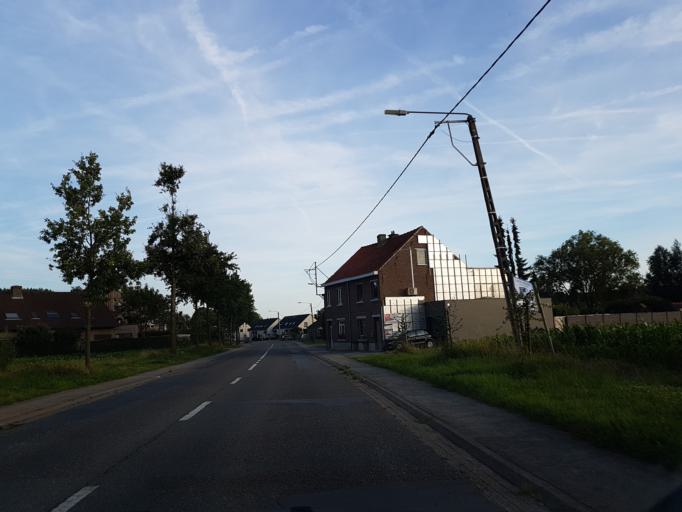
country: BE
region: Flanders
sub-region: Provincie Vlaams-Brabant
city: Merchtem
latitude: 50.9695
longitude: 4.2315
